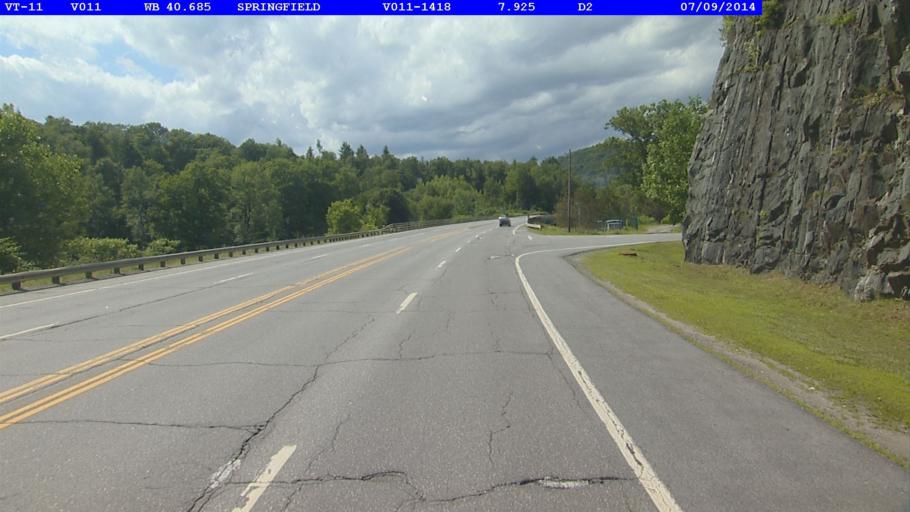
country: US
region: New Hampshire
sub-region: Sullivan County
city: Charlestown
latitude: 43.2656
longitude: -72.4424
